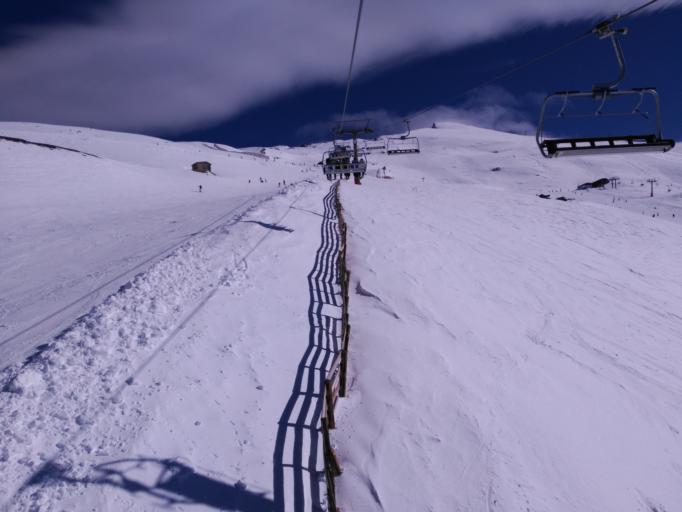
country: ES
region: Andalusia
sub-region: Provincia de Granada
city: Capileira
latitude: 37.0666
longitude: -3.3757
